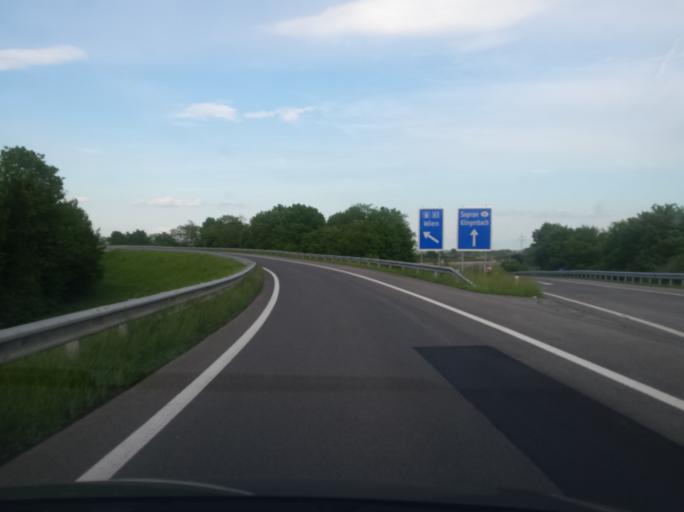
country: AT
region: Burgenland
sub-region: Eisenstadt-Umgebung
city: Wulkaprodersdorf
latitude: 47.8130
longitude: 16.4950
